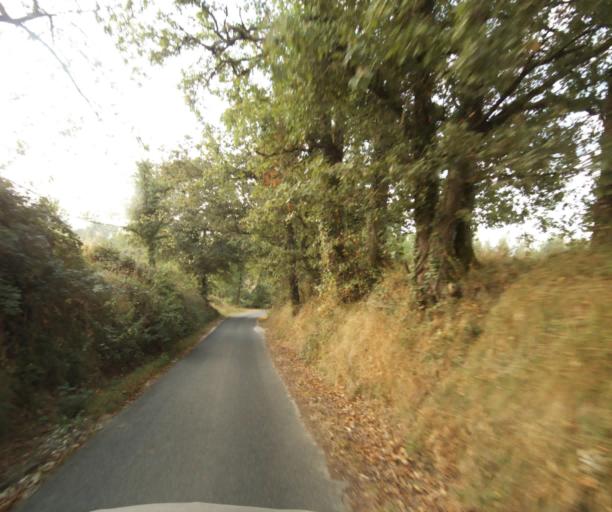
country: FR
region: Aquitaine
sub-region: Departement de la Gironde
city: Creon
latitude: 44.7751
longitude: -0.3370
